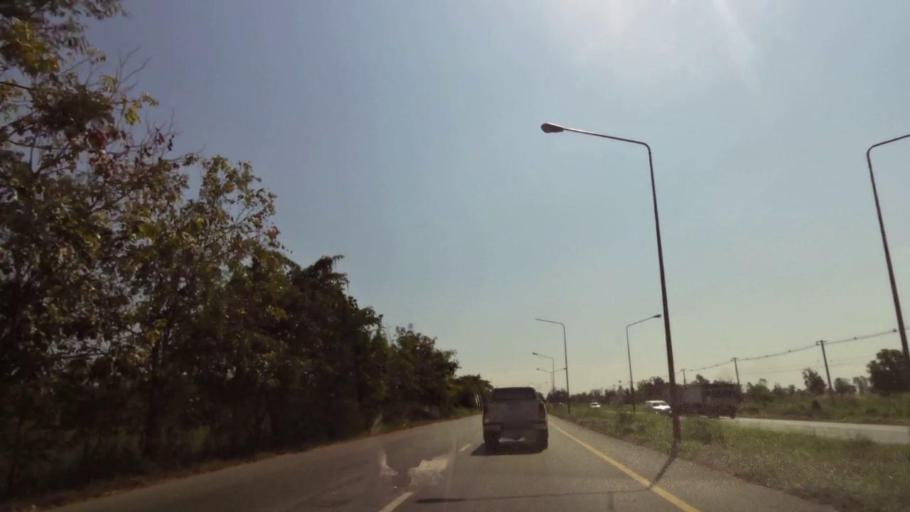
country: TH
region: Nakhon Sawan
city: Kao Liao
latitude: 15.8652
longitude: 100.1167
